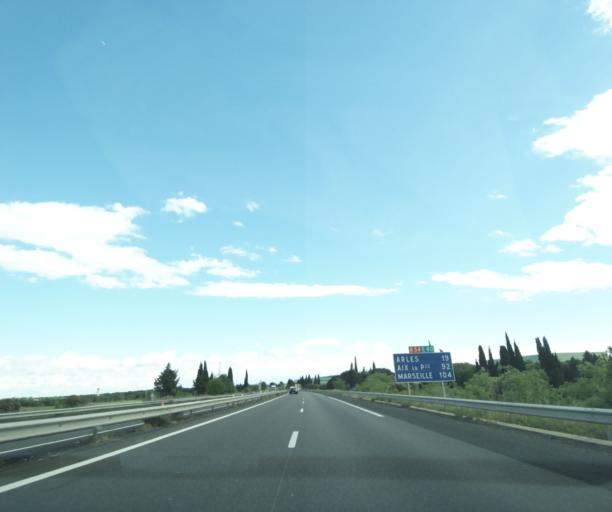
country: FR
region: Languedoc-Roussillon
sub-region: Departement du Gard
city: Garons
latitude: 43.7521
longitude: 4.4312
